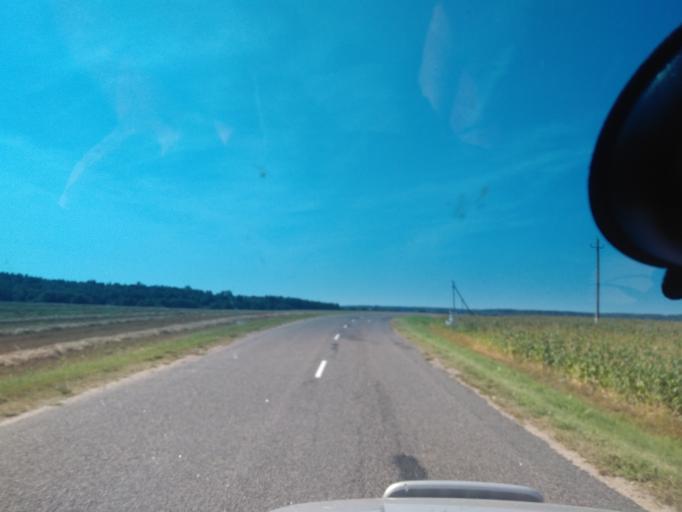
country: BY
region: Minsk
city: Kapyl'
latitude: 53.2189
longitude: 27.1481
